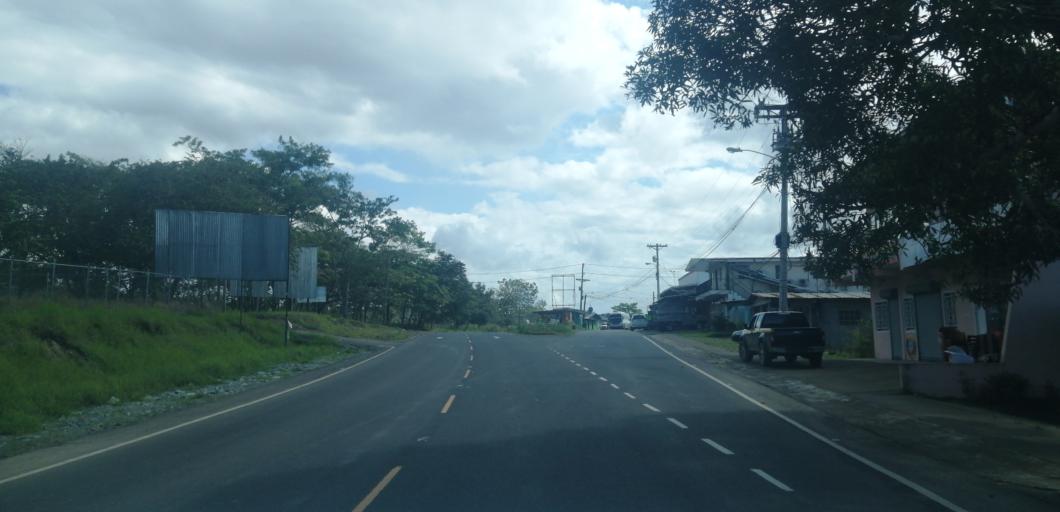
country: PA
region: Panama
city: Canita
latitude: 9.2213
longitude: -78.8919
